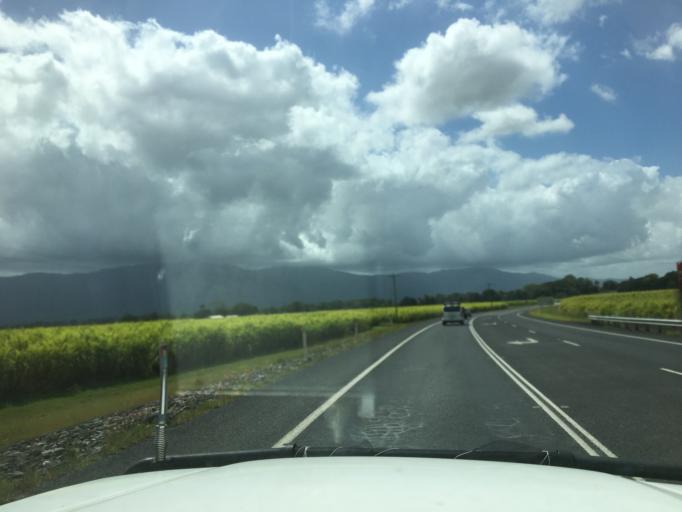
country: AU
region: Queensland
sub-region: Cairns
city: Woree
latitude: -17.1016
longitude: 145.7915
